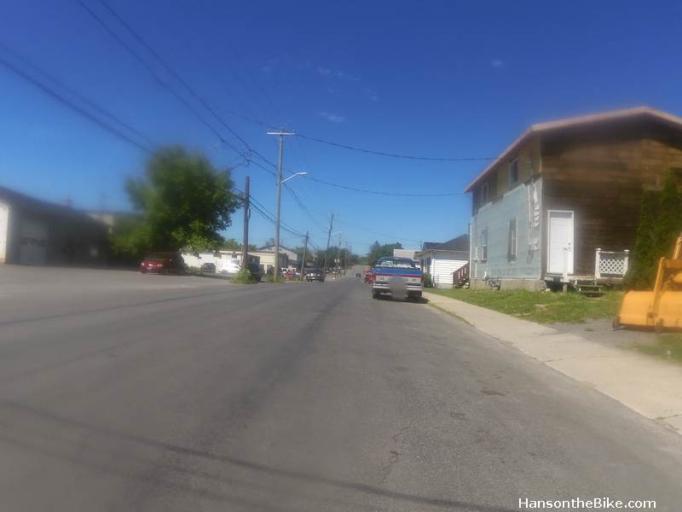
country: CA
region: Ontario
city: Kingston
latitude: 44.2530
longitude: -76.4871
